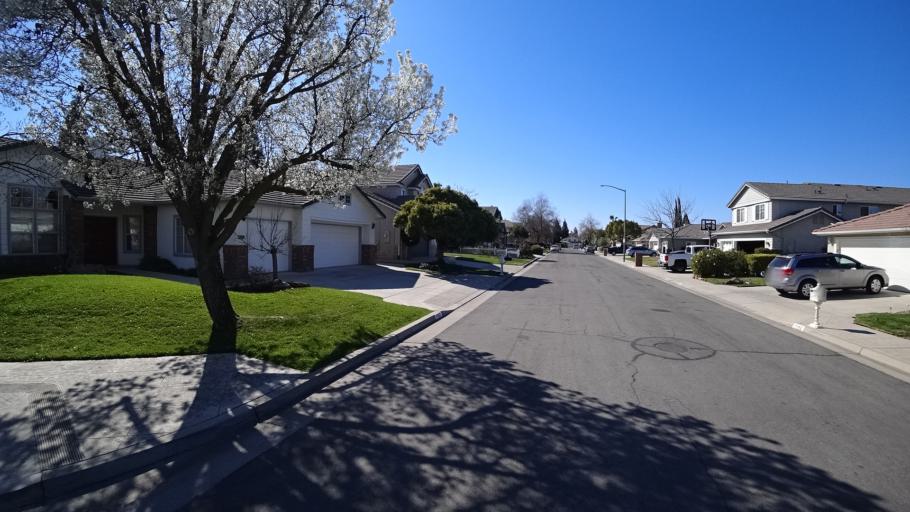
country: US
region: California
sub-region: Fresno County
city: Clovis
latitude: 36.8640
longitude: -119.7416
